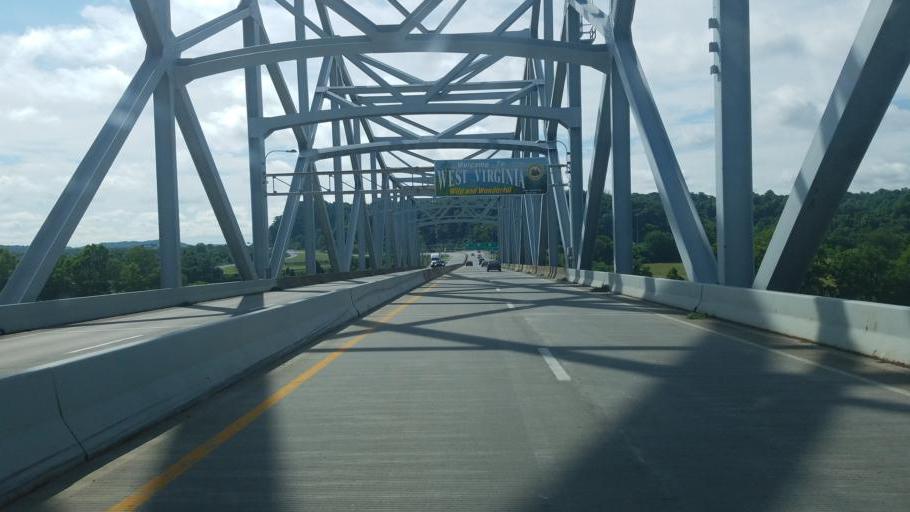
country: US
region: West Virginia
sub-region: Mason County
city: Point Pleasant
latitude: 38.8342
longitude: -82.1469
